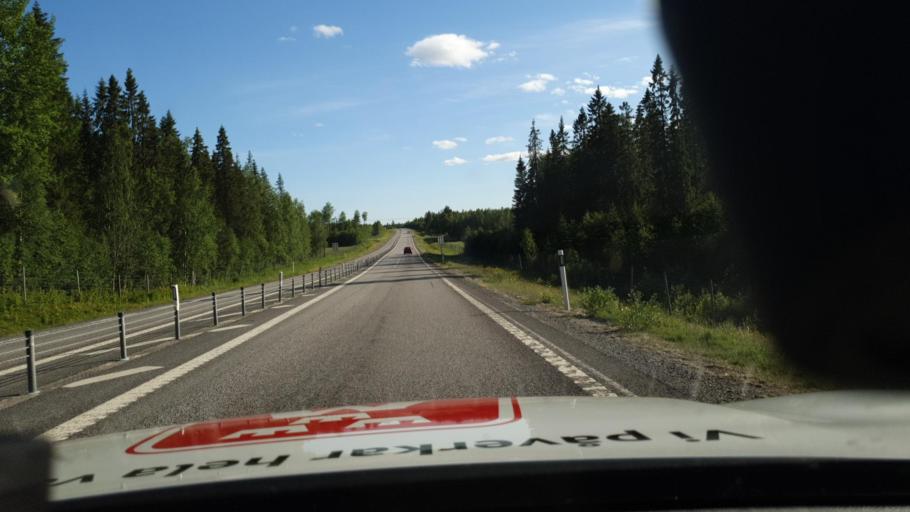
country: SE
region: Norrbotten
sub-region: Lulea Kommun
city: Lulea
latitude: 65.7019
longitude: 22.1203
